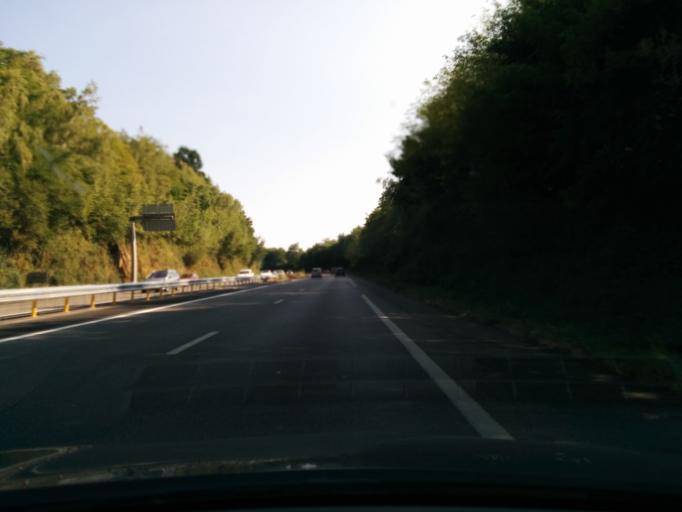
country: FR
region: Limousin
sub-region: Departement de la Haute-Vienne
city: Condat-sur-Vienne
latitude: 45.8023
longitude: 1.2964
